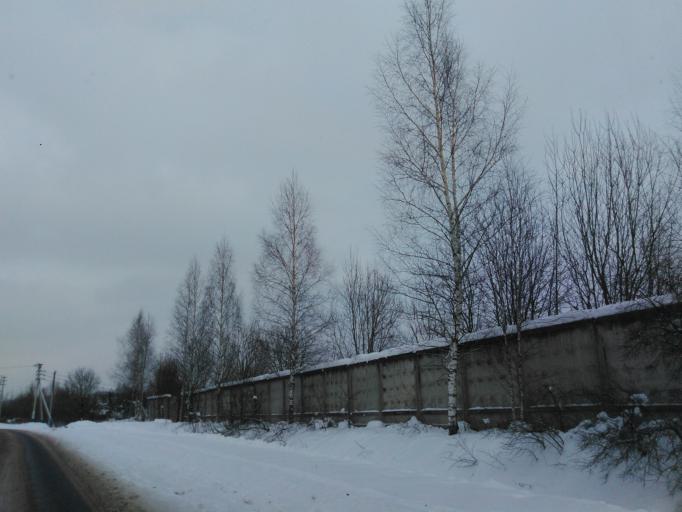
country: RU
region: Moskovskaya
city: Yakhroma
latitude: 56.2742
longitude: 37.4907
